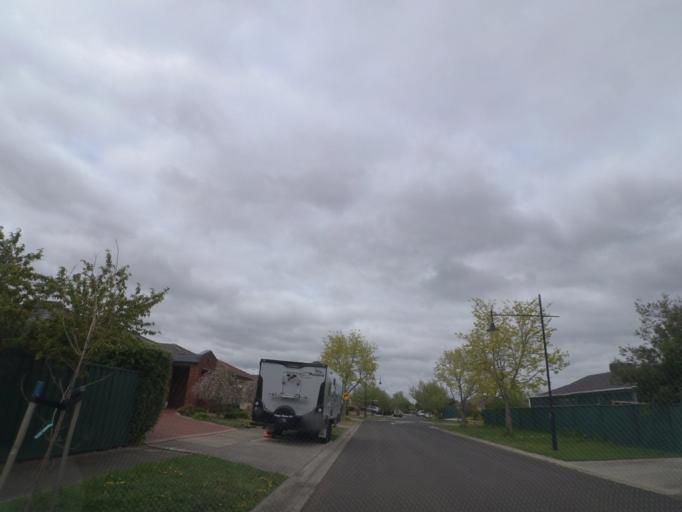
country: AU
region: Victoria
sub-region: Melton
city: Caroline Springs
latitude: -37.7437
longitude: 144.7482
